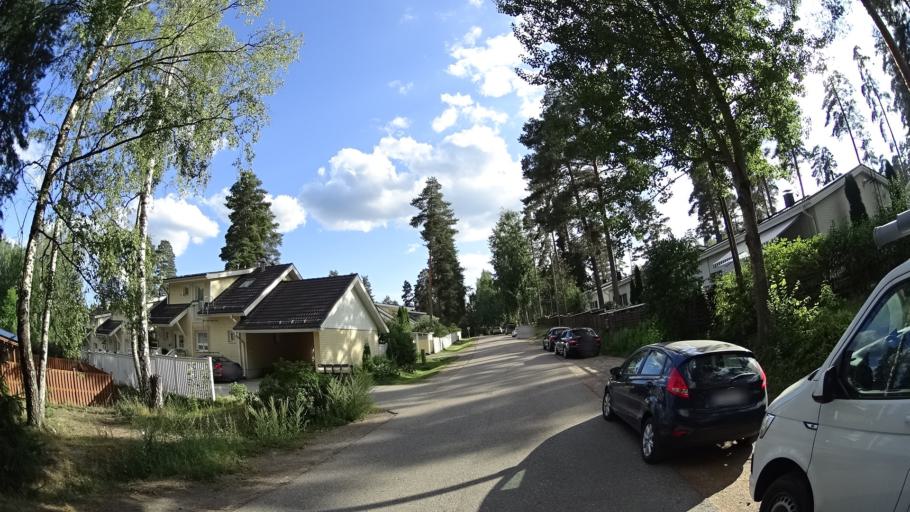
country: FI
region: Uusimaa
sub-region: Helsinki
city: Vihti
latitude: 60.3476
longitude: 24.3292
